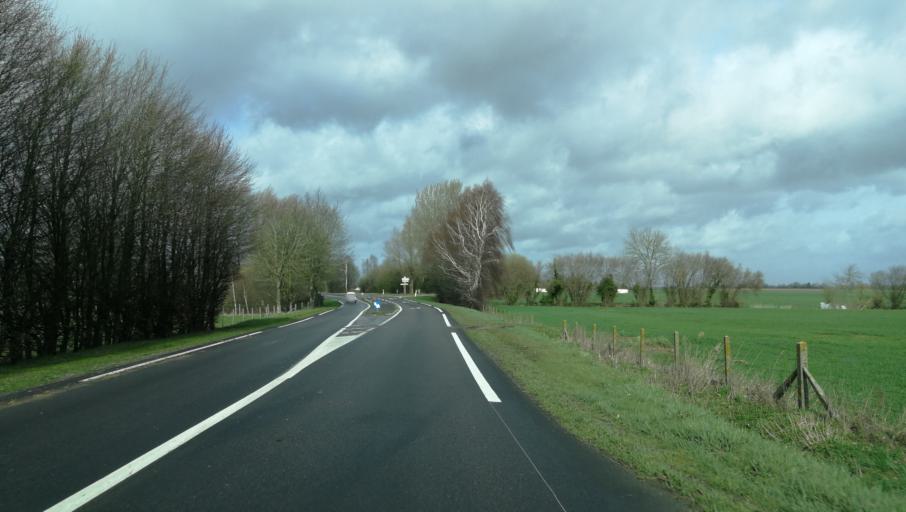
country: FR
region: Haute-Normandie
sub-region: Departement de l'Eure
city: Beuzeville
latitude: 49.3093
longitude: 0.3862
